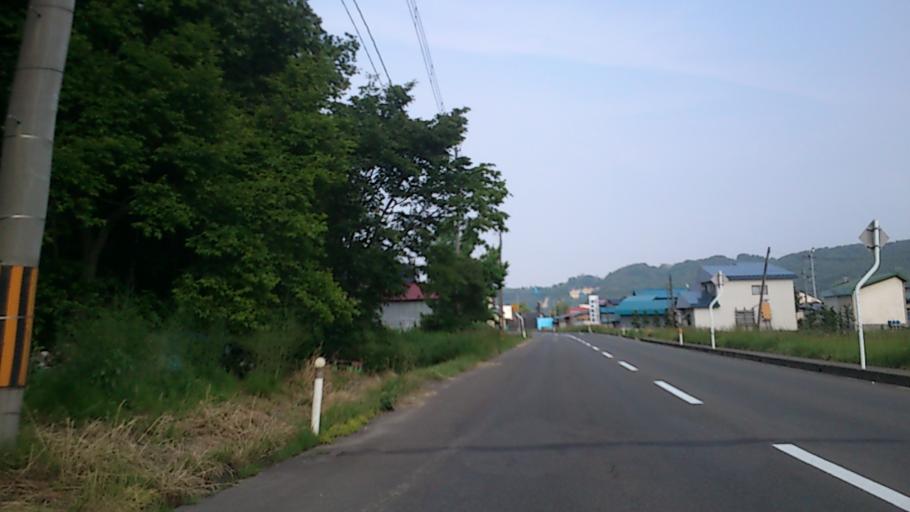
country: JP
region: Aomori
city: Hirosaki
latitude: 40.5907
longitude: 140.3308
